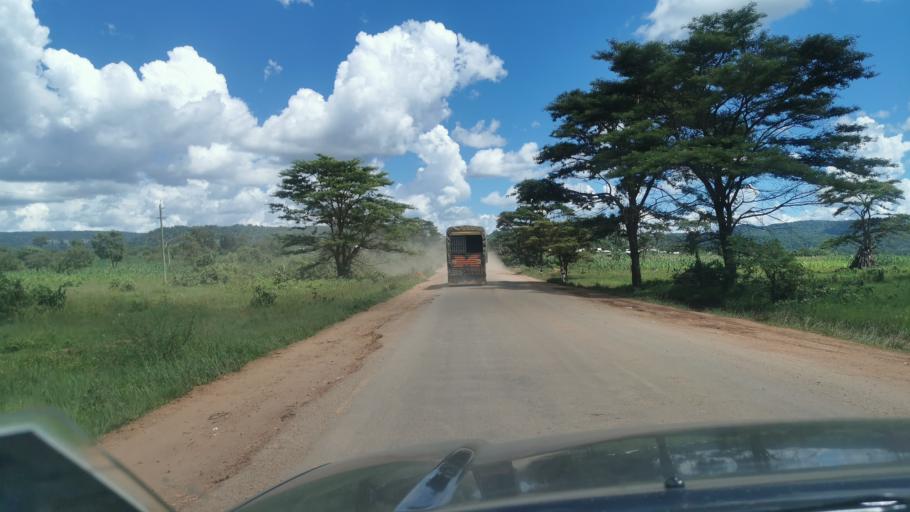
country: TZ
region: Kagera
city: Biharamulo
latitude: -2.8907
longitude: 31.1445
